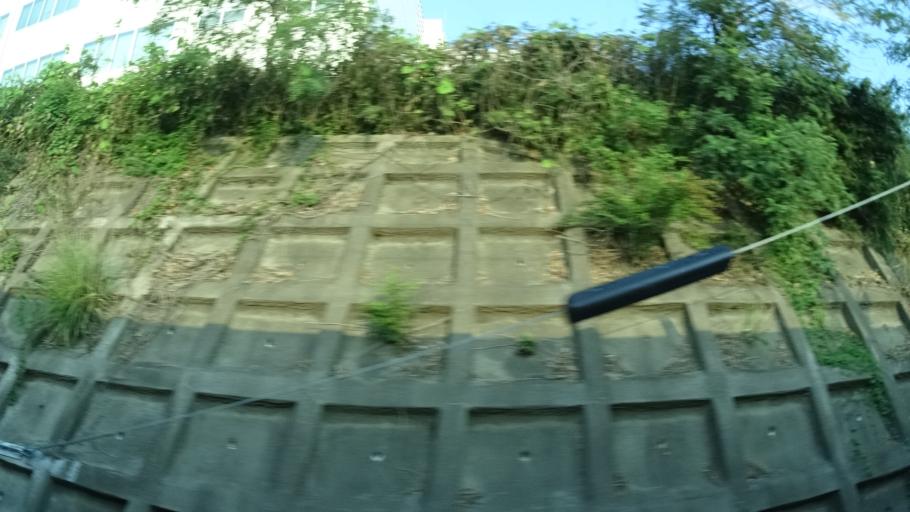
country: JP
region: Ibaraki
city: Funaishikawa
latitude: 36.5087
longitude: 140.6174
